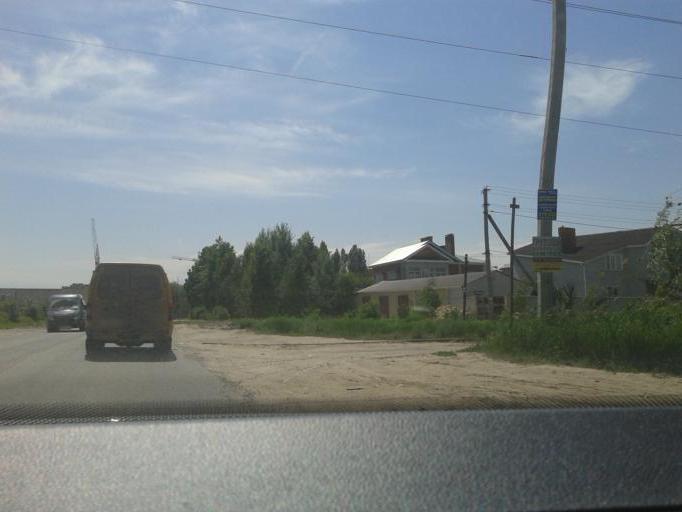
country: RU
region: Volgograd
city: Gorodishche
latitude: 48.7699
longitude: 44.5069
